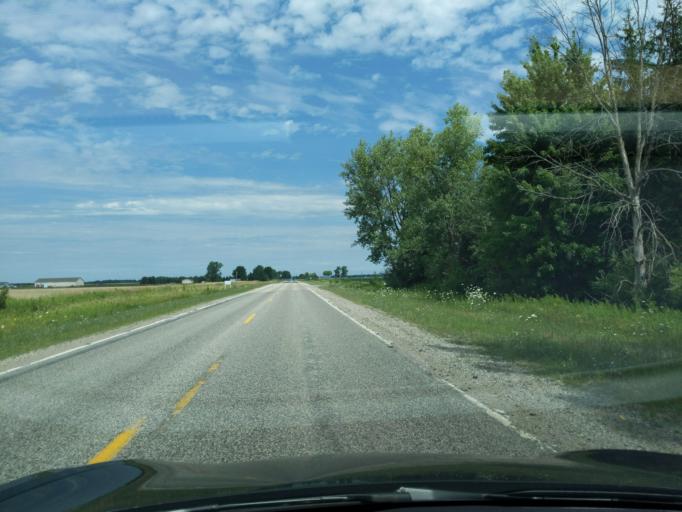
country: US
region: Michigan
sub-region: Gratiot County
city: Breckenridge
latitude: 43.4620
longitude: -84.3699
